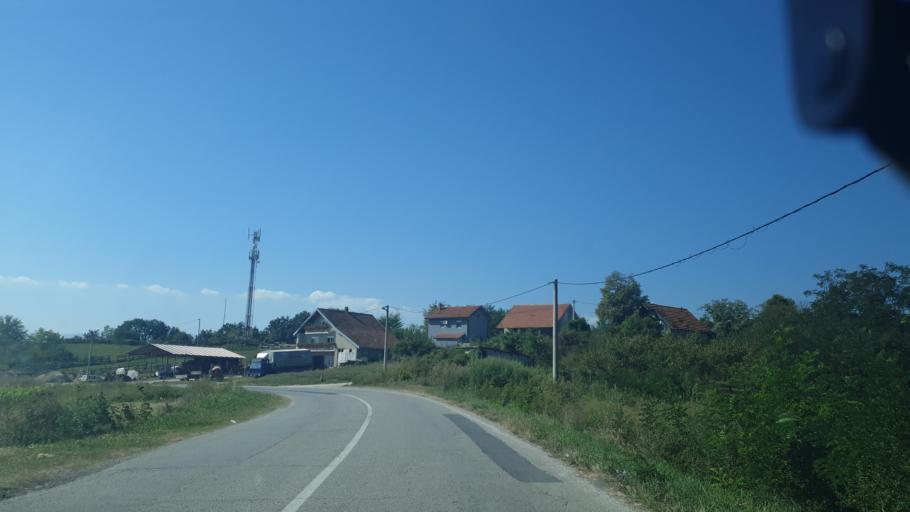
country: RS
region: Central Serbia
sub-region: Kolubarski Okrug
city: Mionica
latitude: 44.2615
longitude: 20.0991
